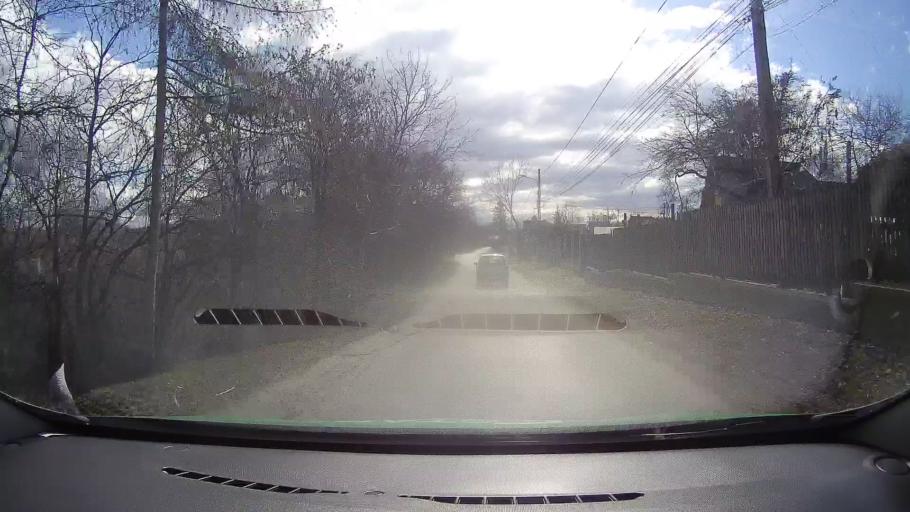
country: RO
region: Dambovita
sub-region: Oras Pucioasa
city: Pucioasa
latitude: 45.0658
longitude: 25.4242
